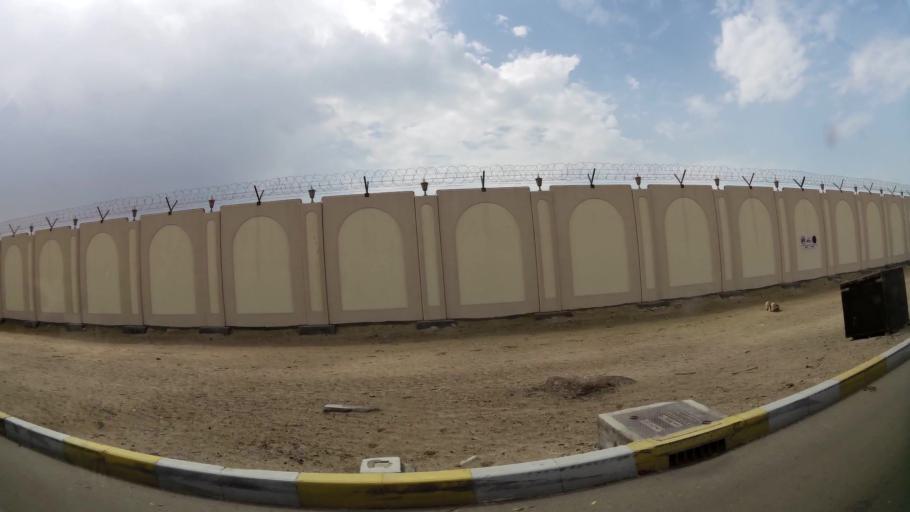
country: AE
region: Abu Dhabi
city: Abu Dhabi
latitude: 24.4204
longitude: 54.4724
